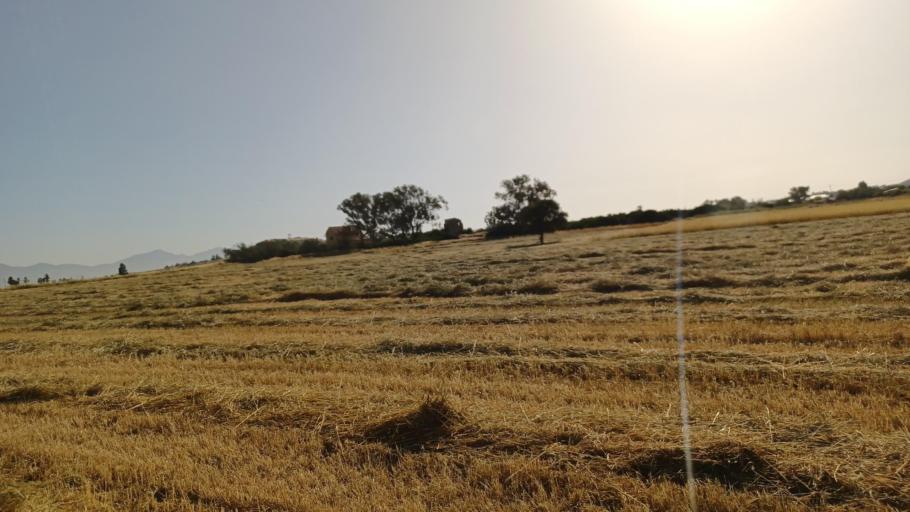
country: CY
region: Lefkosia
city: Mammari
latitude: 35.1670
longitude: 33.2444
